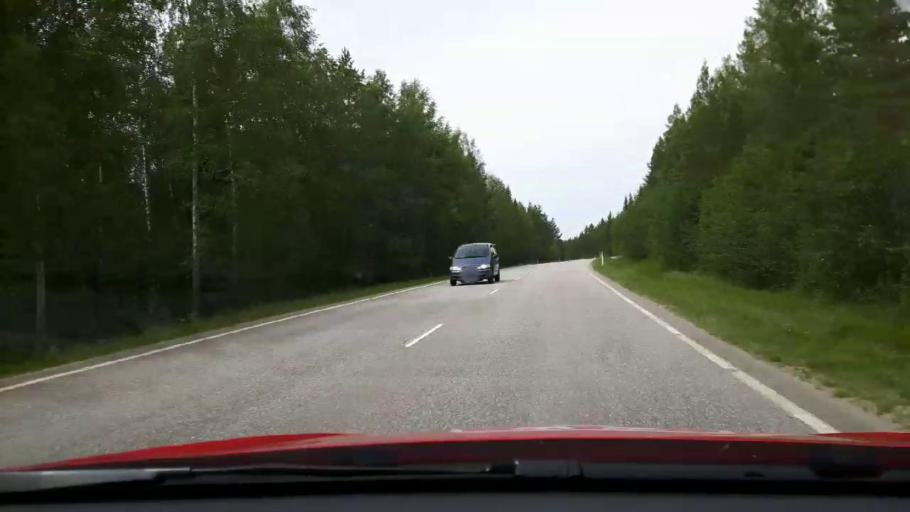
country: SE
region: Jaemtland
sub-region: Harjedalens Kommun
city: Sveg
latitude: 62.1034
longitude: 14.2065
